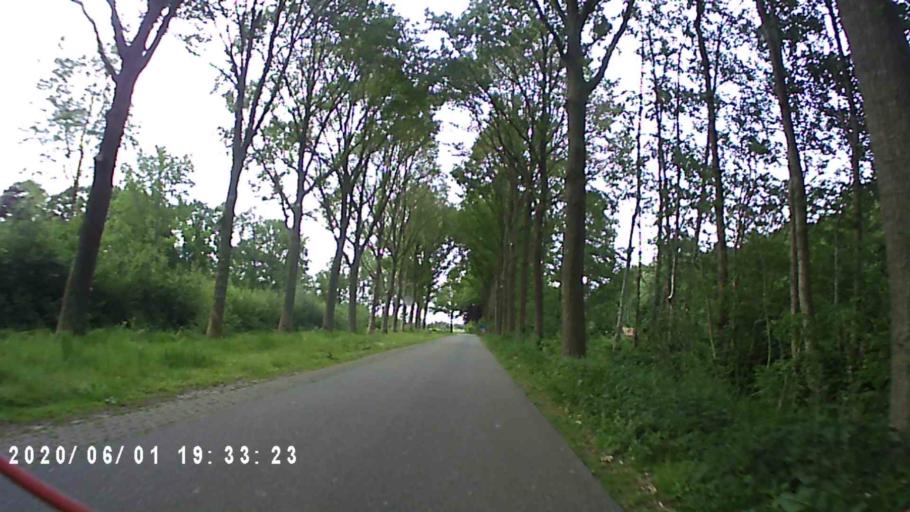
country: NL
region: Friesland
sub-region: Gemeente Achtkarspelen
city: Augustinusga
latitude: 53.2143
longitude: 6.1574
